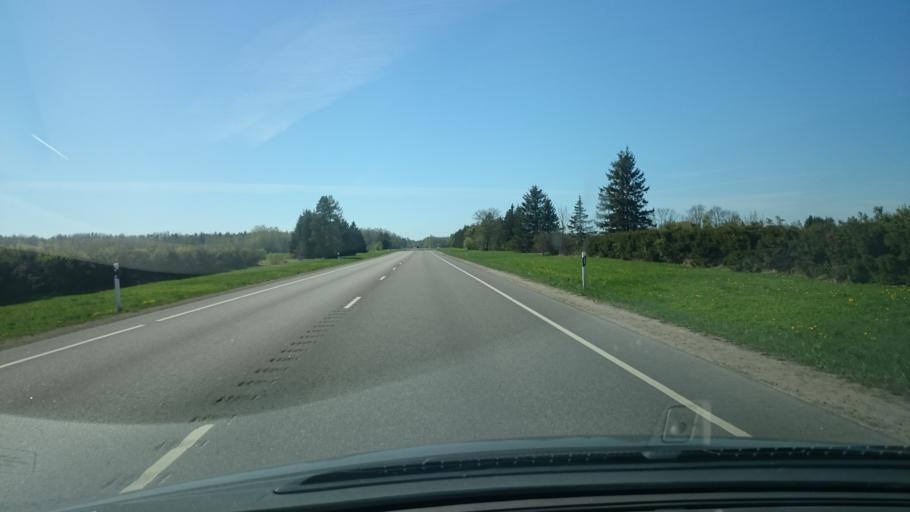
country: EE
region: Ida-Virumaa
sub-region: Sillamaee linn
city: Sillamae
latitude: 59.3923
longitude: 27.6772
